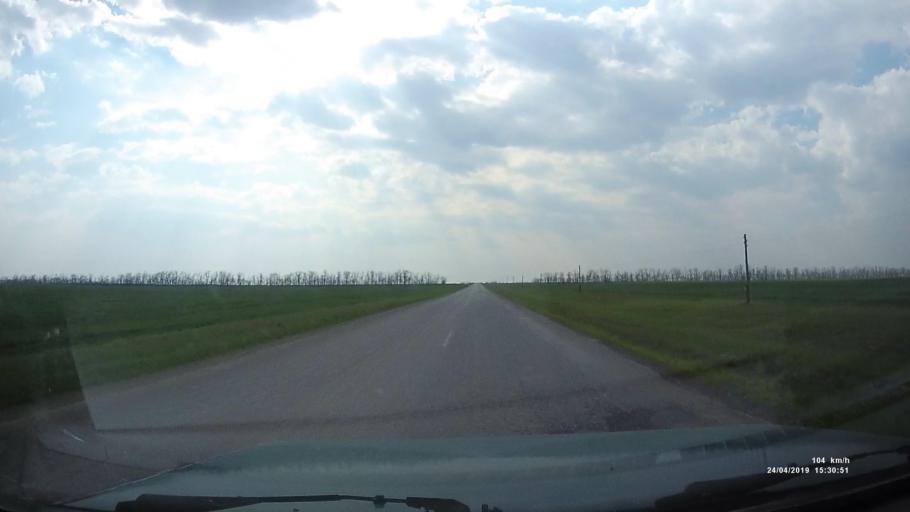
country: RU
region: Rostov
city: Remontnoye
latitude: 46.5994
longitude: 42.9982
